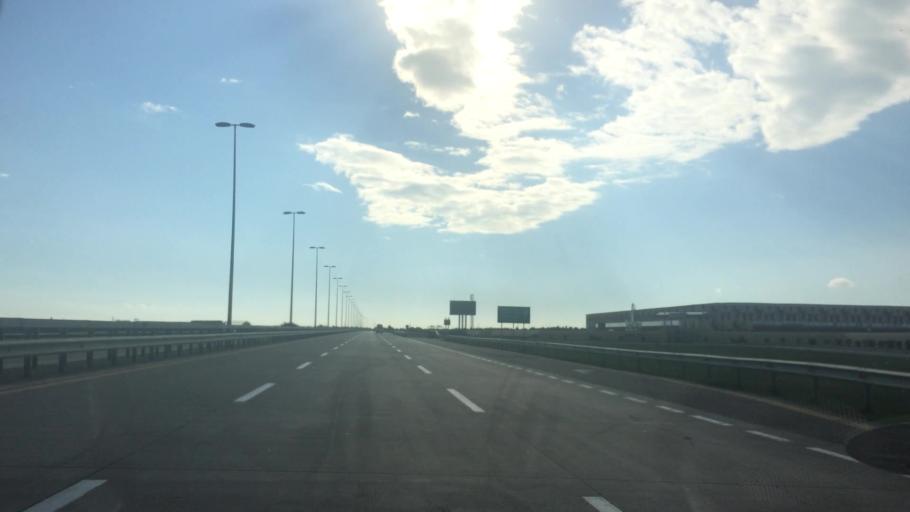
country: AZ
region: Baki
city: Hovsan
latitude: 40.3870
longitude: 50.0667
